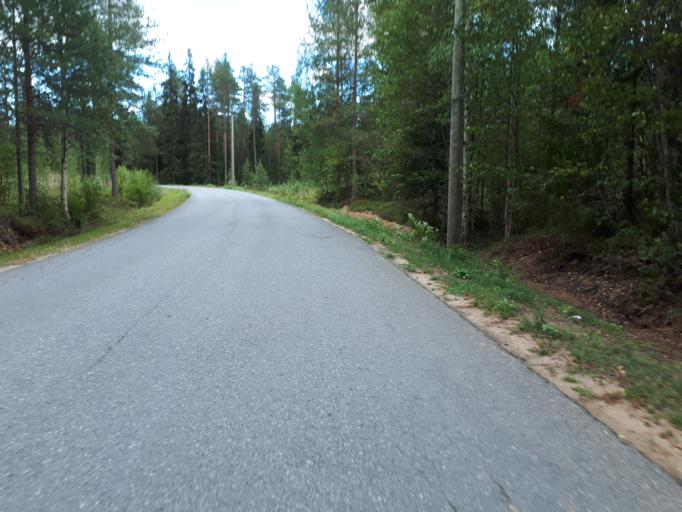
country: FI
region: Northern Ostrobothnia
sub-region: Oulunkaari
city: Ii
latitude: 65.3260
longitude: 25.3927
